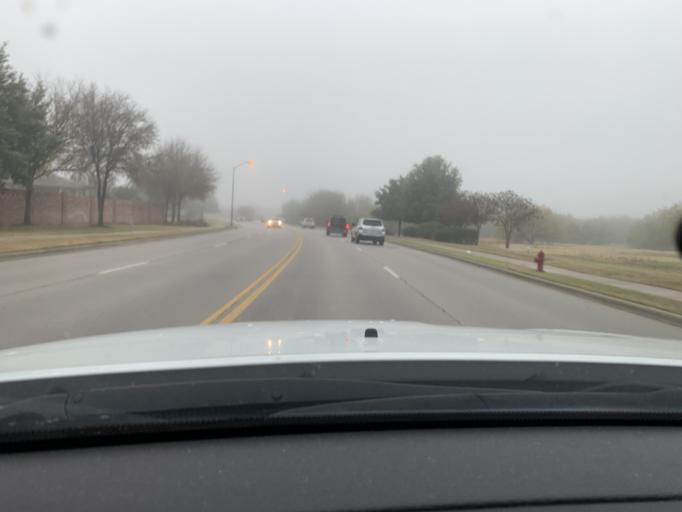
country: US
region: Texas
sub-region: Williamson County
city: Round Rock
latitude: 30.5661
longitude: -97.6831
